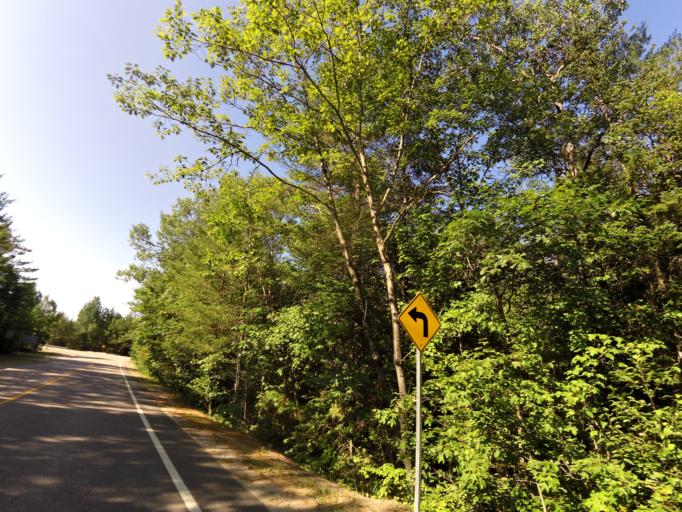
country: CA
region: Ontario
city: Deep River
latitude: 46.1929
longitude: -77.6851
